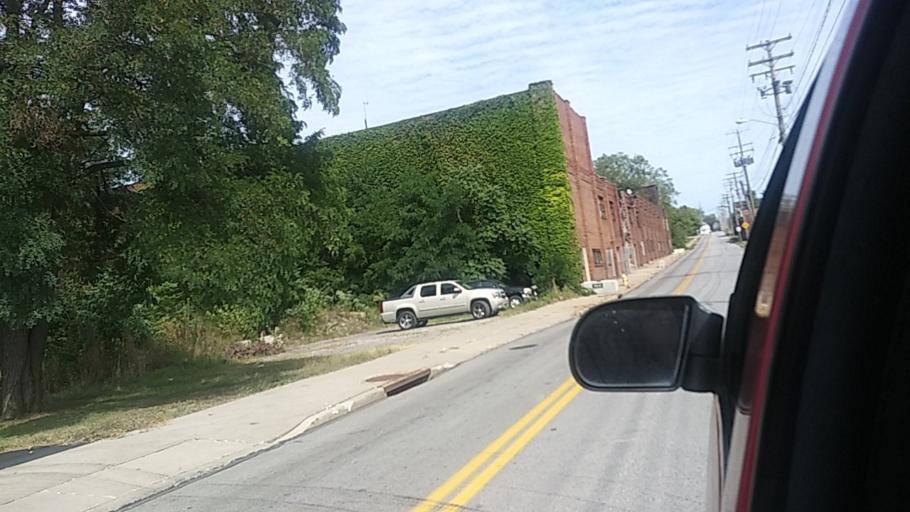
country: US
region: Ohio
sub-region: Summit County
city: Akron
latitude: 41.0554
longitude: -81.5164
